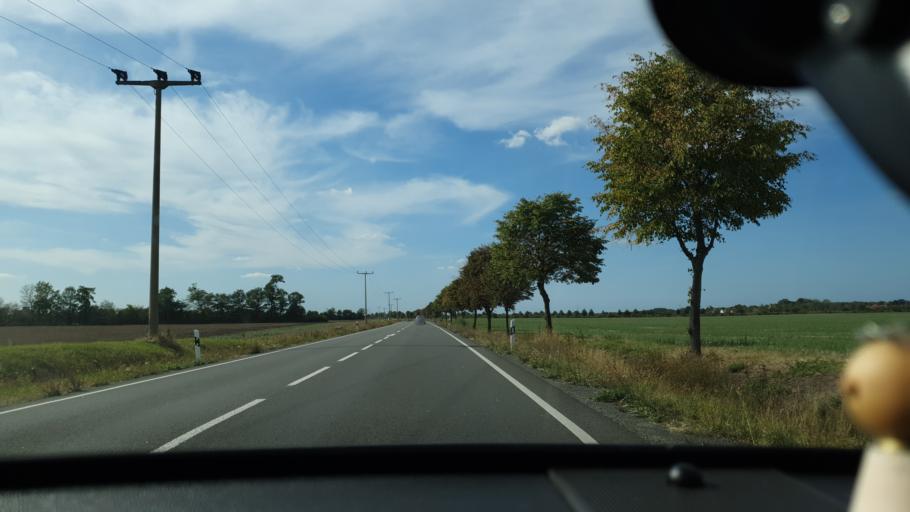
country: DE
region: Saxony
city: Jesewitz
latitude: 51.4572
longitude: 12.5427
